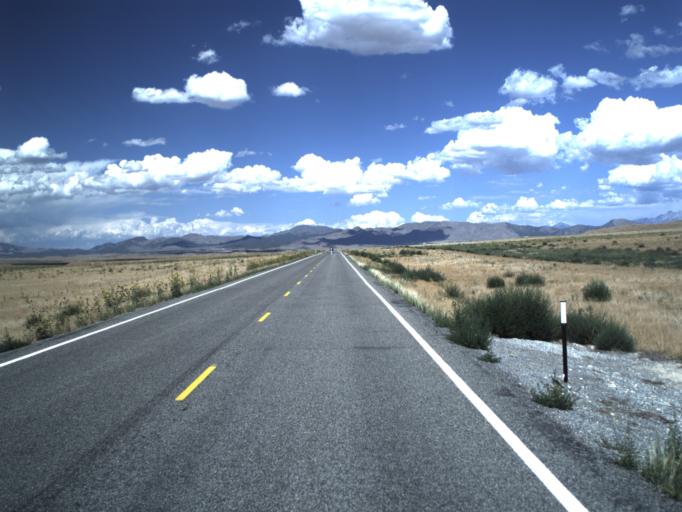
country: US
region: Utah
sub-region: Millard County
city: Delta
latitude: 39.6588
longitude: -112.2832
